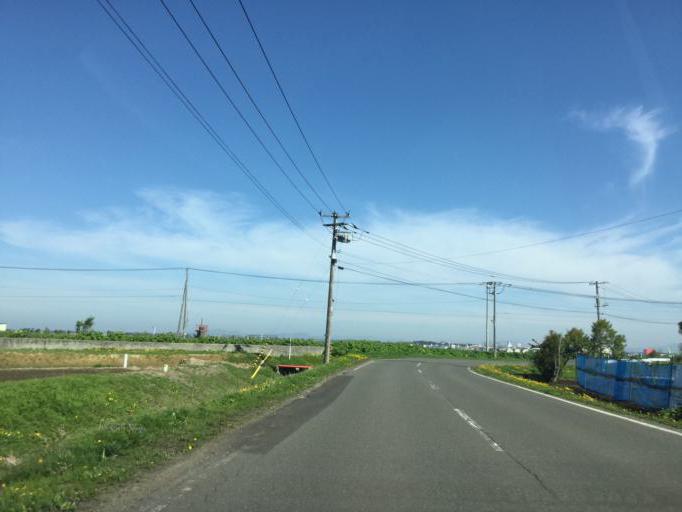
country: JP
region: Hokkaido
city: Iwamizawa
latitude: 43.1717
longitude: 141.7469
